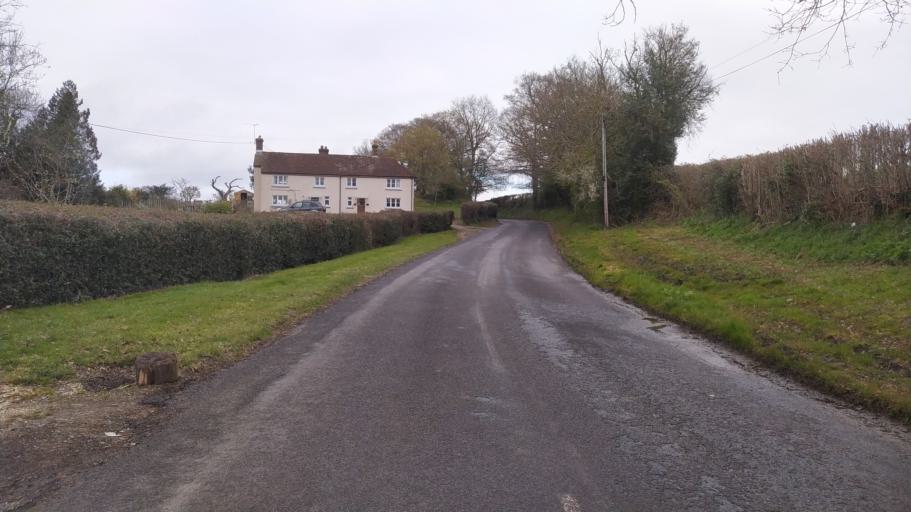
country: GB
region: England
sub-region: West Sussex
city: Petworth
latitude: 51.0034
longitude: -0.6095
